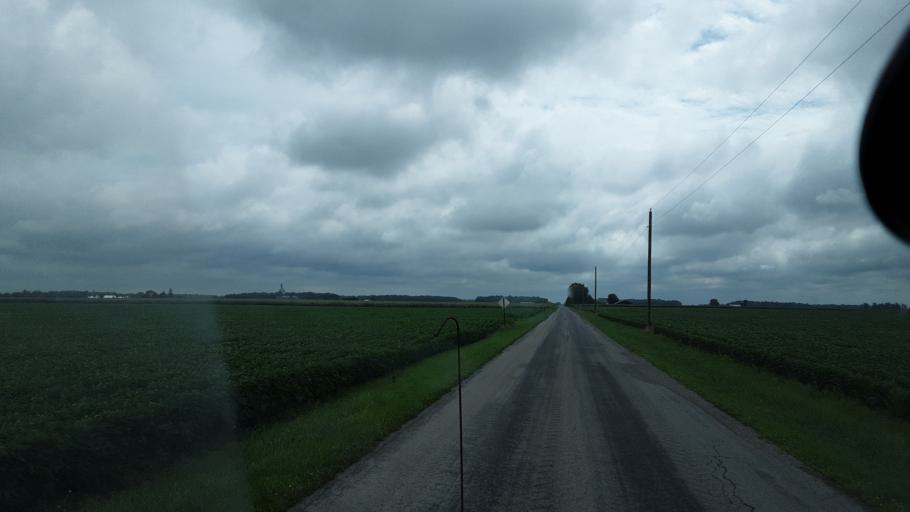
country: US
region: Indiana
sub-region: Wells County
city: Ossian
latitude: 40.8521
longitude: -85.0997
